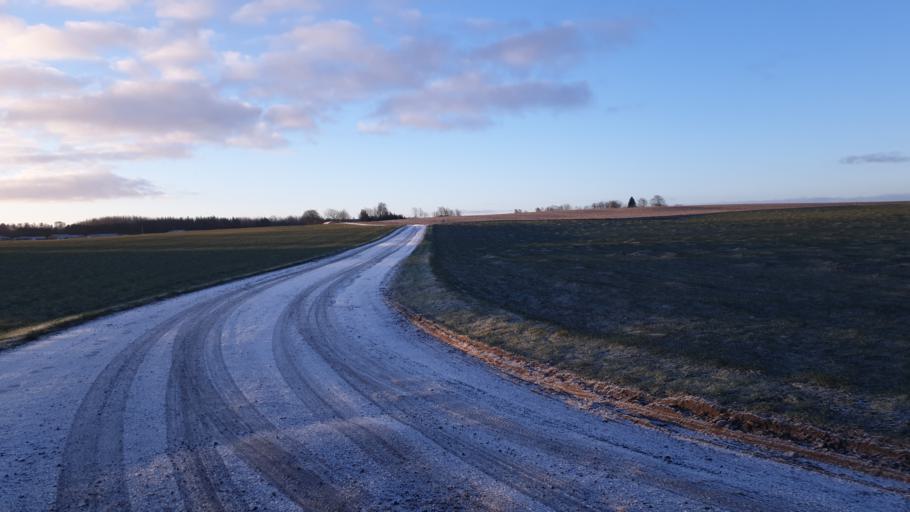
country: DK
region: Central Jutland
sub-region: Hedensted Kommune
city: Hedensted
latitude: 55.8187
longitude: 9.7010
